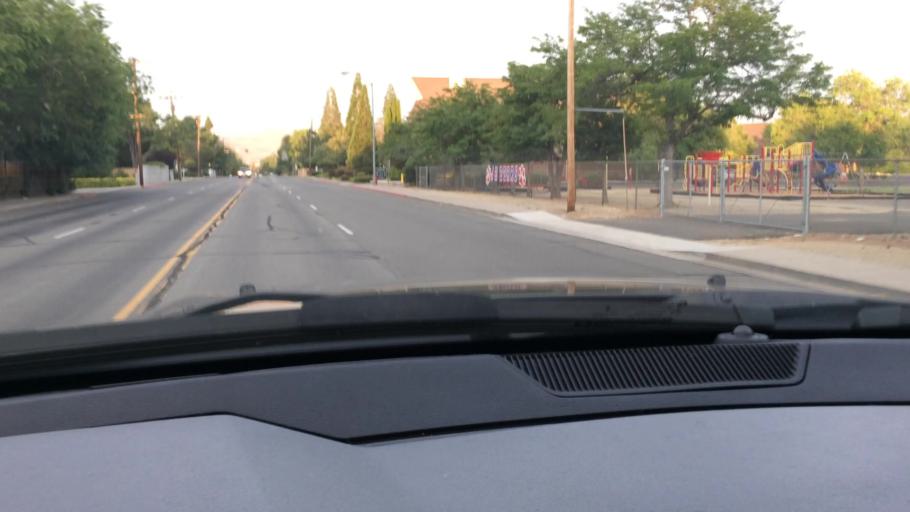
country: US
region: Nevada
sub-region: Washoe County
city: Reno
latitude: 39.5054
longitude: -119.8257
